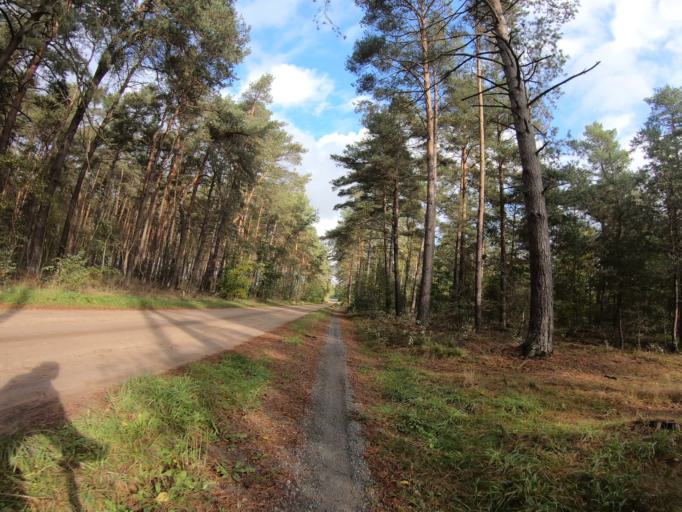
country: DE
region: Lower Saxony
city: Wesendorf
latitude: 52.5790
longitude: 10.5702
